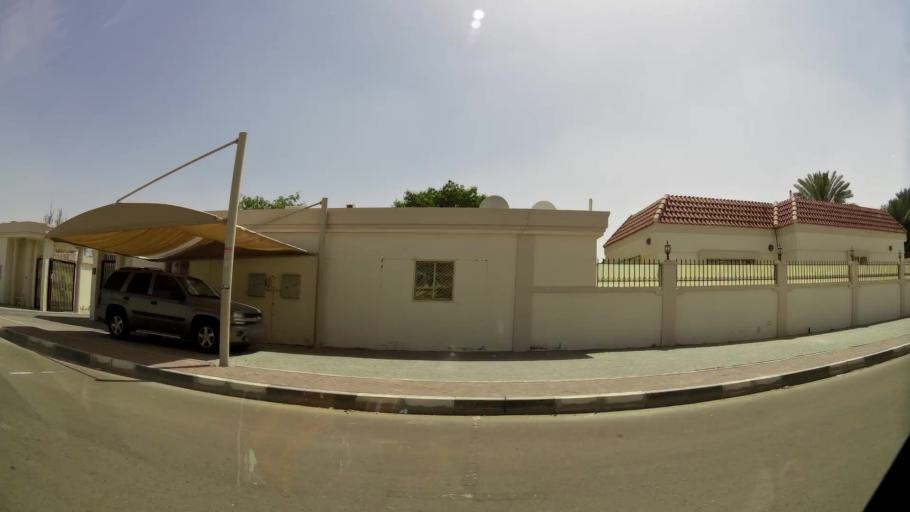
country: AE
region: Abu Dhabi
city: Al Ain
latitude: 24.2327
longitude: 55.7102
